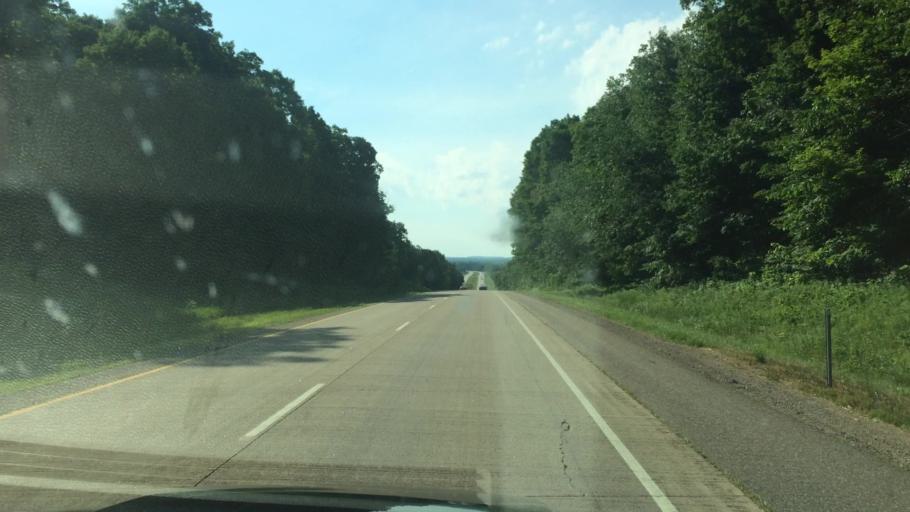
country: US
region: Wisconsin
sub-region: Shawano County
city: Wittenberg
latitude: 44.8207
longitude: -89.0560
